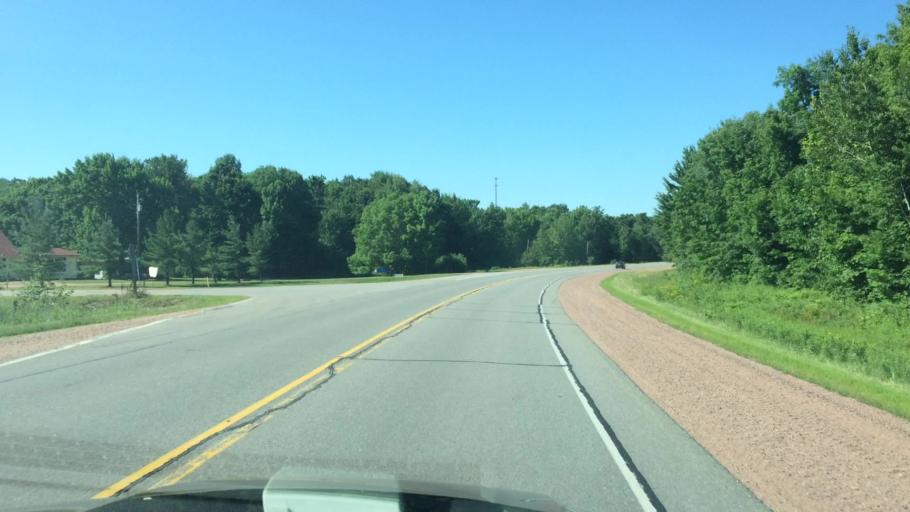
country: US
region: Wisconsin
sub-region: Marathon County
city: Stratford
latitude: 44.7363
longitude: -90.0799
